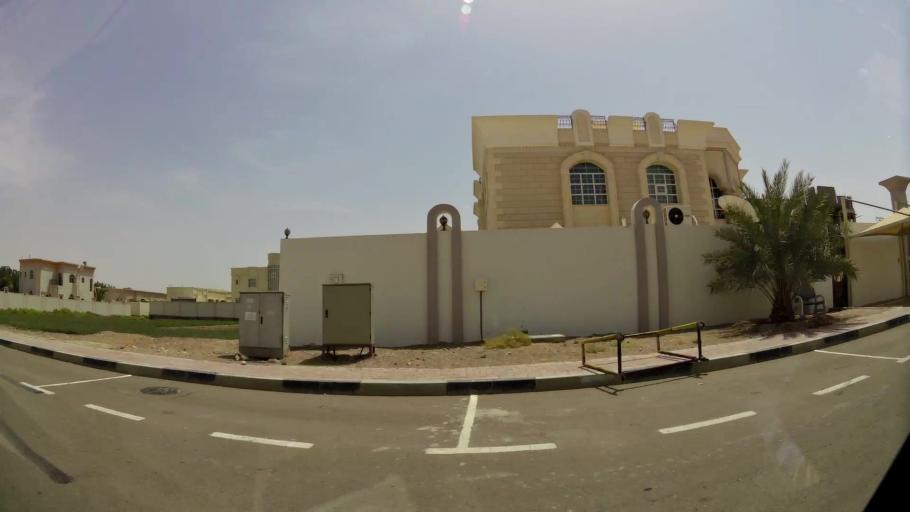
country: AE
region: Abu Dhabi
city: Al Ain
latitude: 24.1772
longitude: 55.7084
